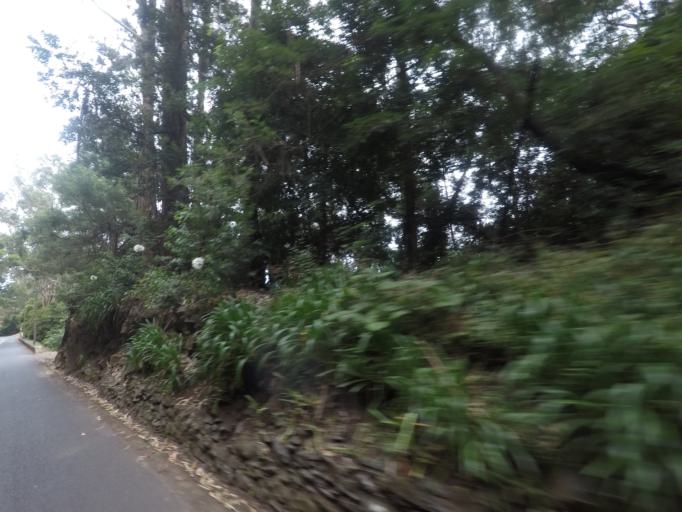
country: PT
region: Madeira
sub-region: Funchal
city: Nossa Senhora do Monte
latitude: 32.6662
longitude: -16.8746
